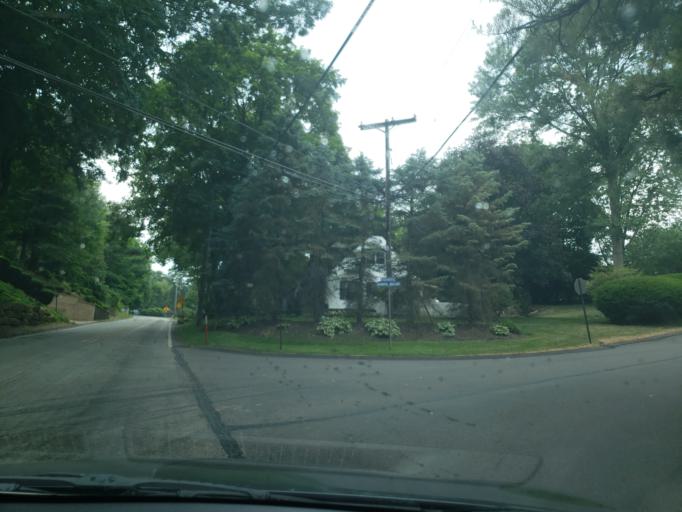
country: US
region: Pennsylvania
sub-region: Allegheny County
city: Ben Avon
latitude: 40.5154
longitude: -80.0716
